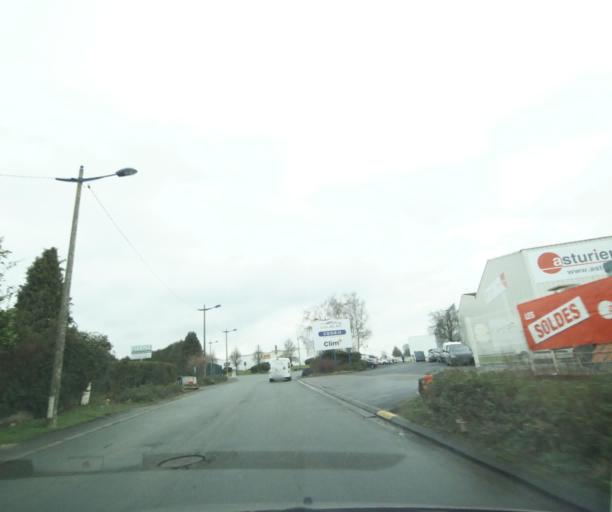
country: FR
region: Nord-Pas-de-Calais
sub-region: Departement du Nord
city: Prouvy
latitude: 50.3340
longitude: 3.4610
